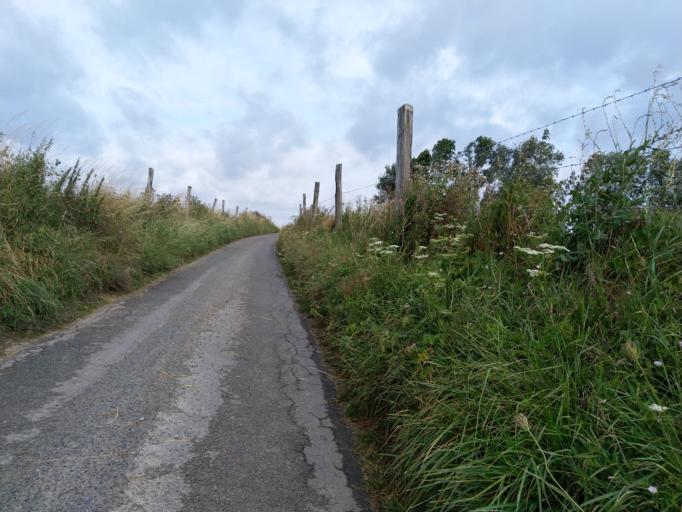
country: BE
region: Wallonia
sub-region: Province du Hainaut
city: Lens
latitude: 50.5534
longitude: 3.8694
